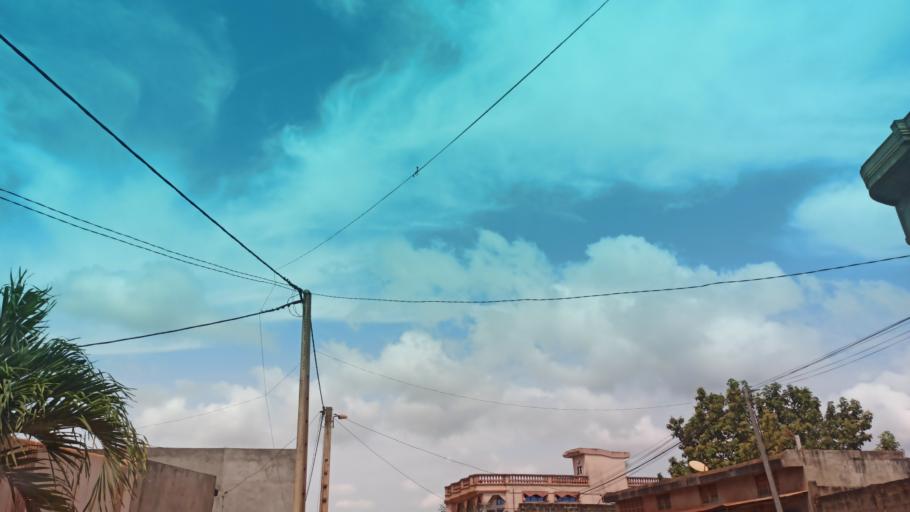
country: BJ
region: Queme
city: Porto-Novo
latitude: 6.5006
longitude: 2.5860
